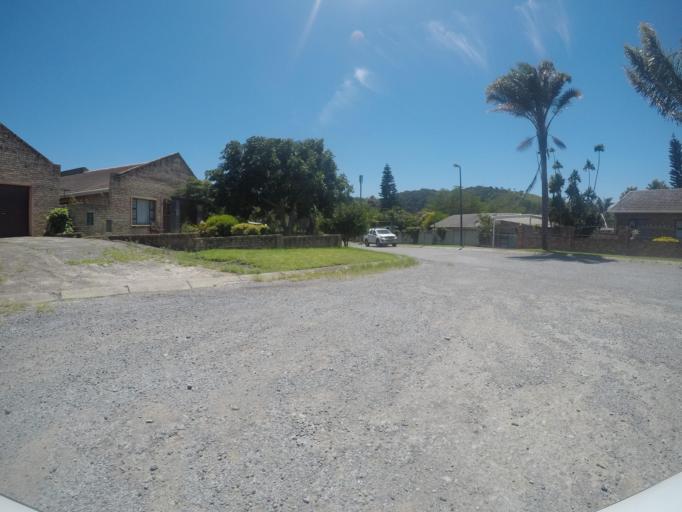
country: ZA
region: Eastern Cape
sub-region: Buffalo City Metropolitan Municipality
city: East London
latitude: -32.9299
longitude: 27.9965
